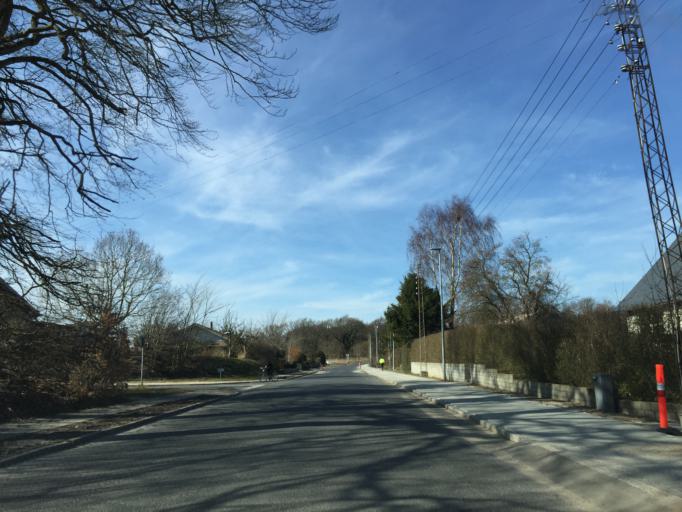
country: DK
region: Central Jutland
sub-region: Silkeborg Kommune
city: Silkeborg
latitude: 56.1944
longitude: 9.5344
